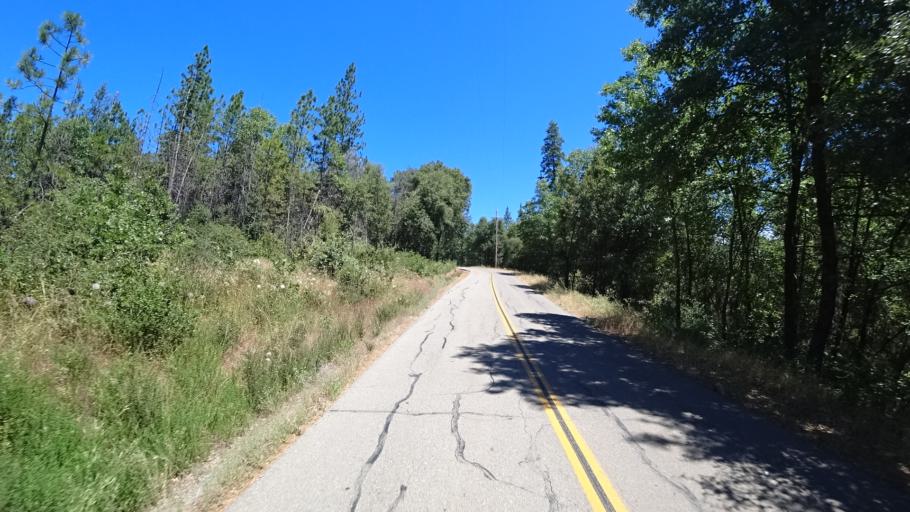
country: US
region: California
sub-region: Amador County
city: Pioneer
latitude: 38.3719
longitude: -120.5212
